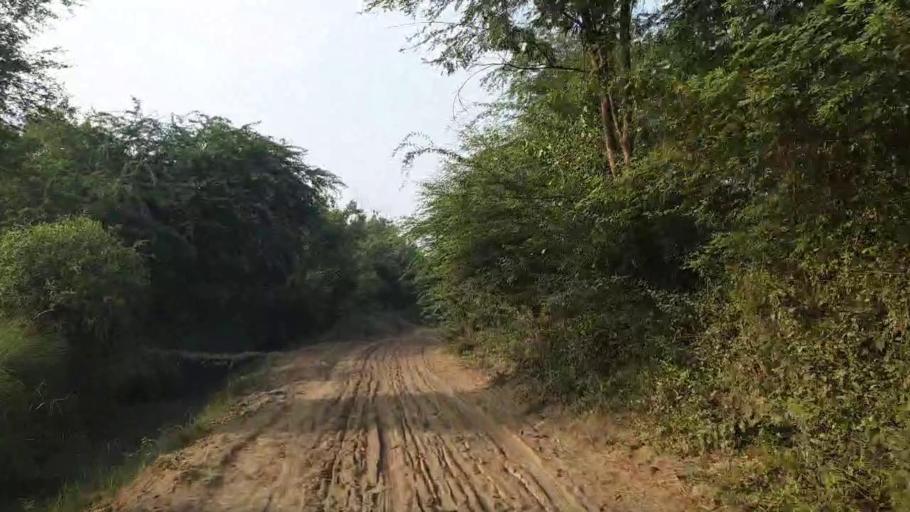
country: PK
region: Sindh
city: Tando Bago
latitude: 24.7805
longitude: 68.8769
